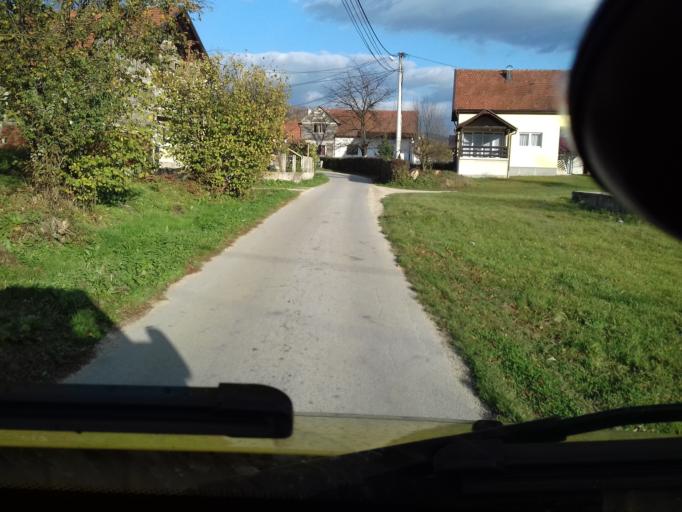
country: BA
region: Federation of Bosnia and Herzegovina
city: Vitez
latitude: 44.1547
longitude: 17.8077
